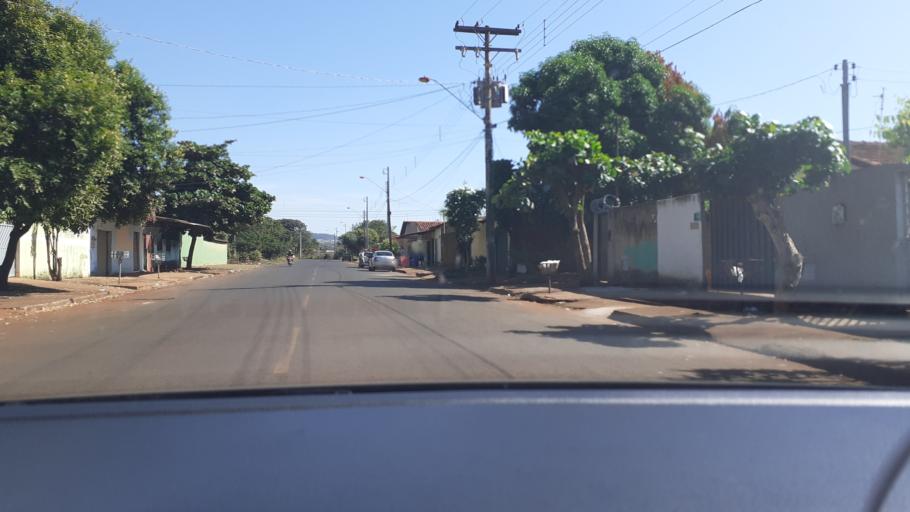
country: BR
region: Goias
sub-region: Itumbiara
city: Itumbiara
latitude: -18.4115
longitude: -49.2572
